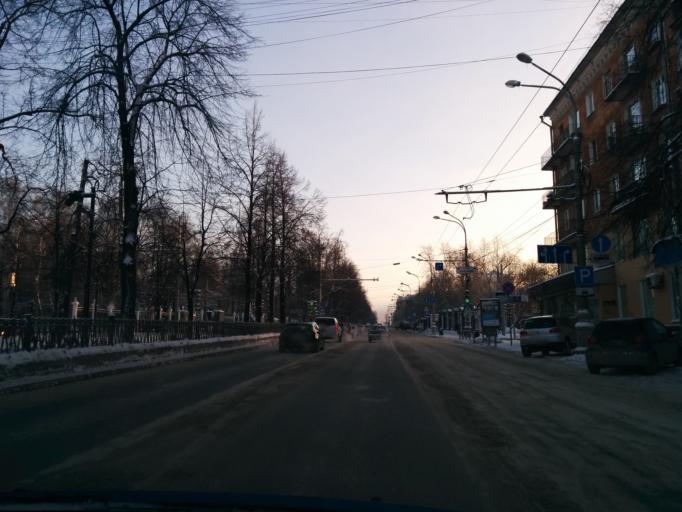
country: RU
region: Perm
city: Perm
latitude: 58.0056
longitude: 56.2441
